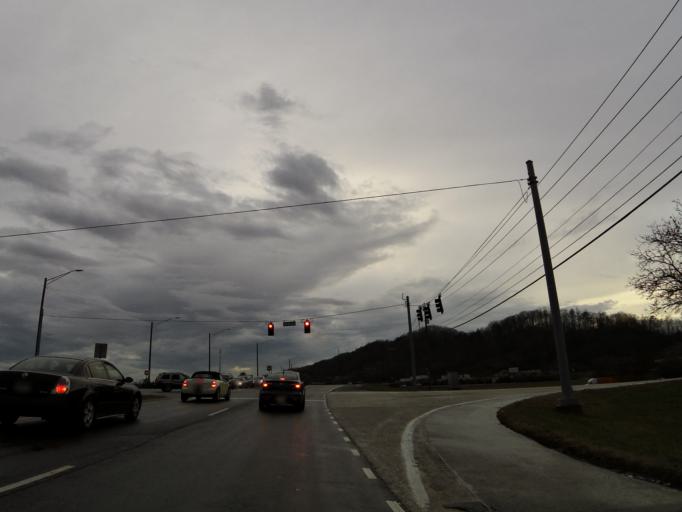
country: US
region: Tennessee
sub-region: Knox County
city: Knoxville
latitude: 36.0255
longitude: -83.9949
